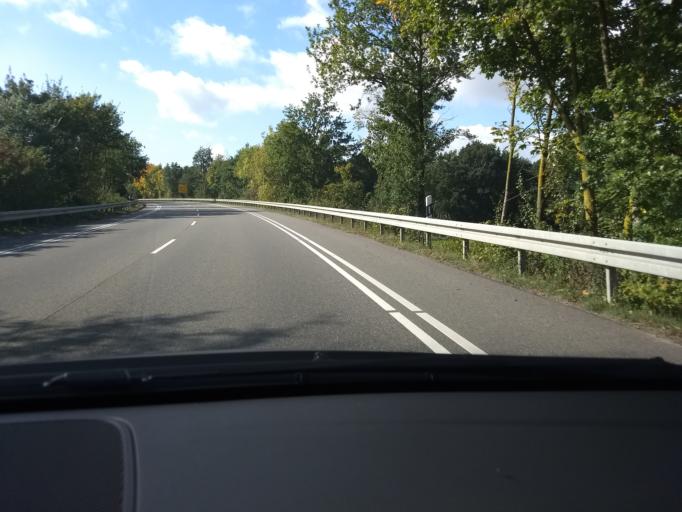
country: DE
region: North Rhine-Westphalia
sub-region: Regierungsbezirk Munster
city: Borken
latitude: 51.8405
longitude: 6.8810
